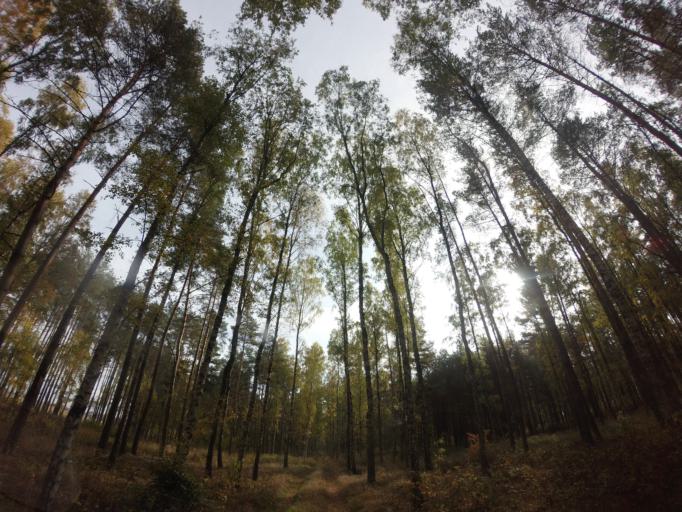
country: PL
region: West Pomeranian Voivodeship
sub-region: Powiat choszczenski
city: Drawno
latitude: 53.2488
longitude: 15.6804
